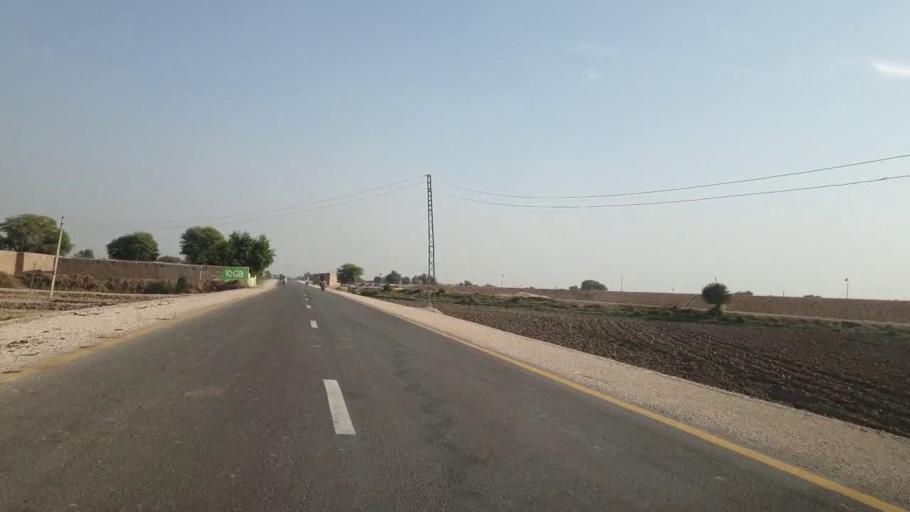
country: PK
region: Sindh
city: Sehwan
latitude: 26.4565
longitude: 67.8069
